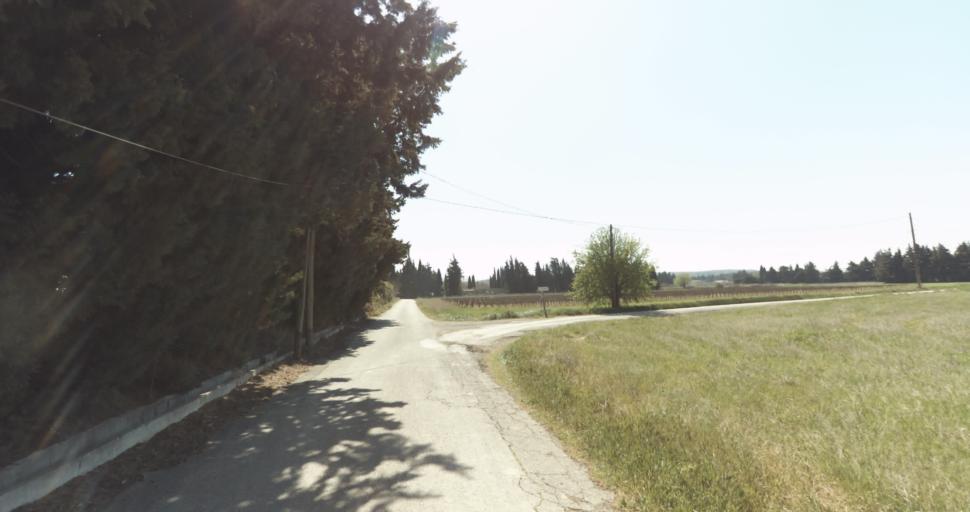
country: FR
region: Provence-Alpes-Cote d'Azur
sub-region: Departement des Bouches-du-Rhone
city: Pelissanne
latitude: 43.6207
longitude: 5.1479
